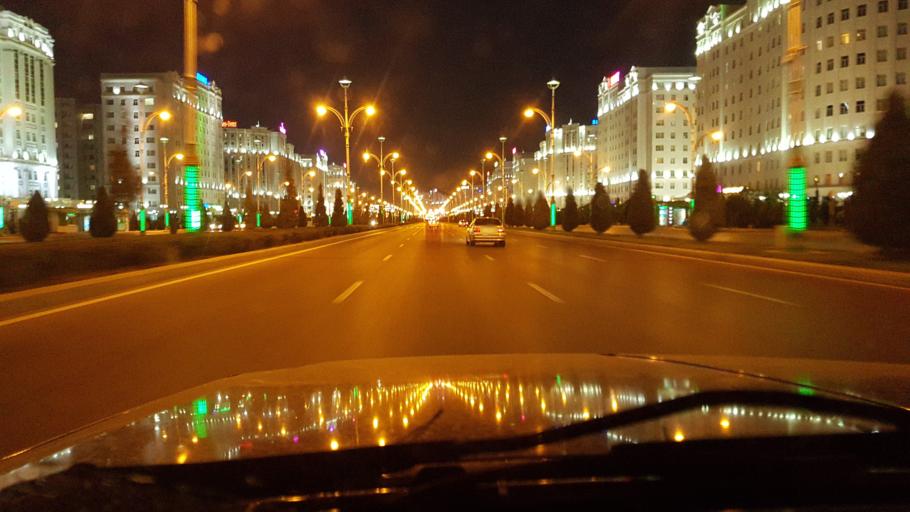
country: TM
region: Ahal
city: Ashgabat
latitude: 37.9038
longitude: 58.3389
